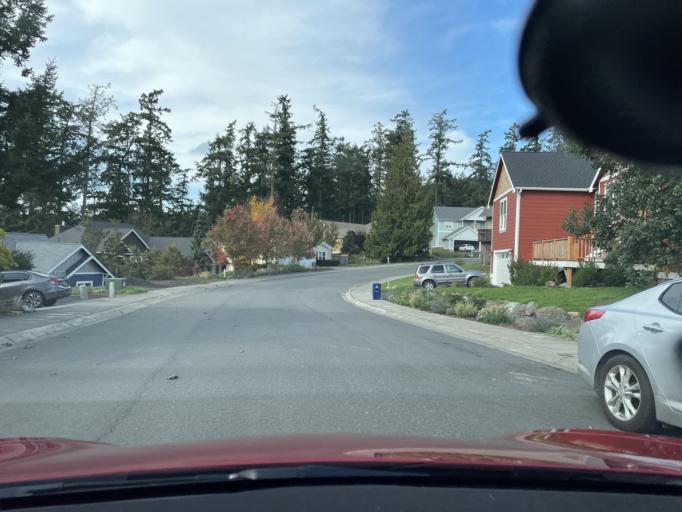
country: US
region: Washington
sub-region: San Juan County
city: Friday Harbor
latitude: 48.5424
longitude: -123.0327
